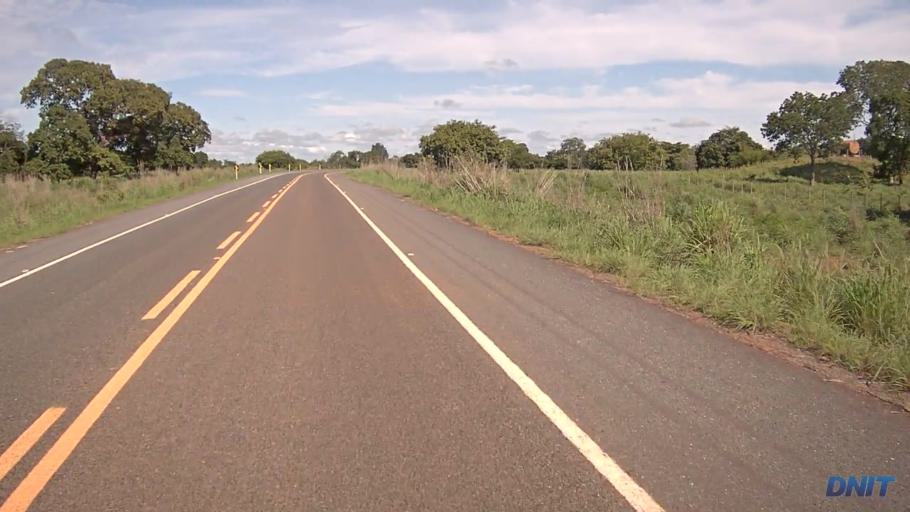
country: BR
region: Goias
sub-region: Sao Miguel Do Araguaia
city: Sao Miguel do Araguaia
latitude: -13.3171
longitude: -50.1659
